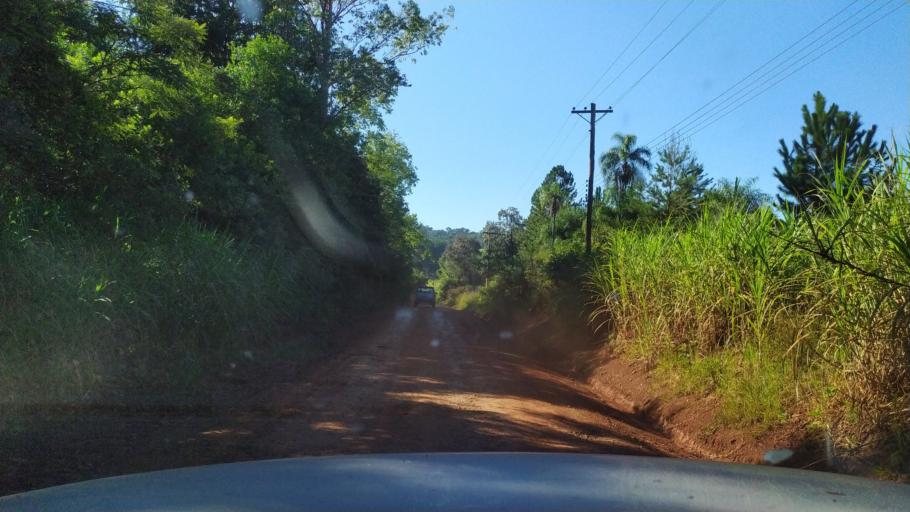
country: AR
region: Misiones
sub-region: Departamento de Montecarlo
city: Montecarlo
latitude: -26.6286
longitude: -54.6905
